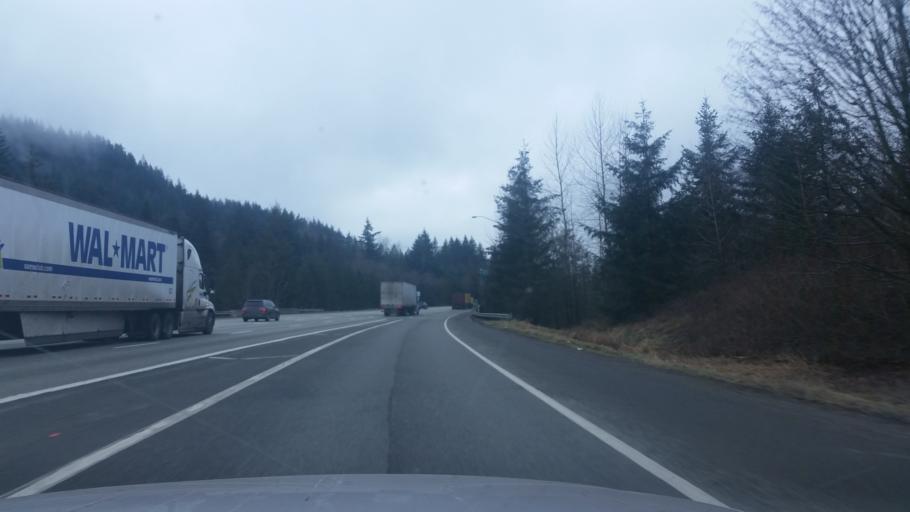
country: US
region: Washington
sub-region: King County
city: Snoqualmie
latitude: 47.5120
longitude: -121.8550
